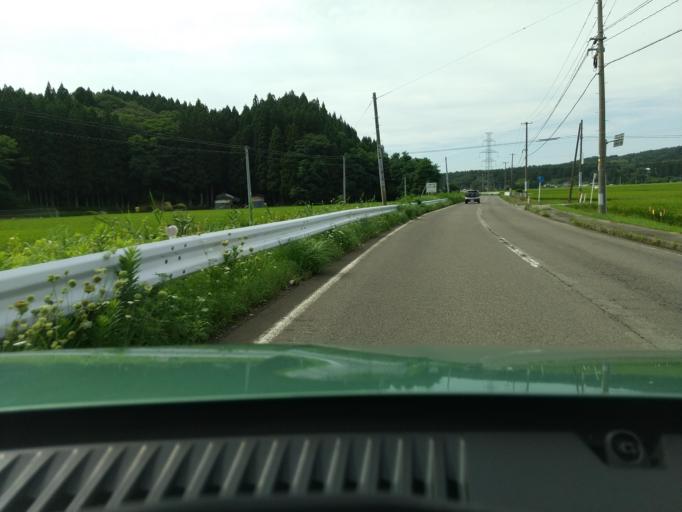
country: JP
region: Akita
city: Akita
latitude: 39.7870
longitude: 140.1215
